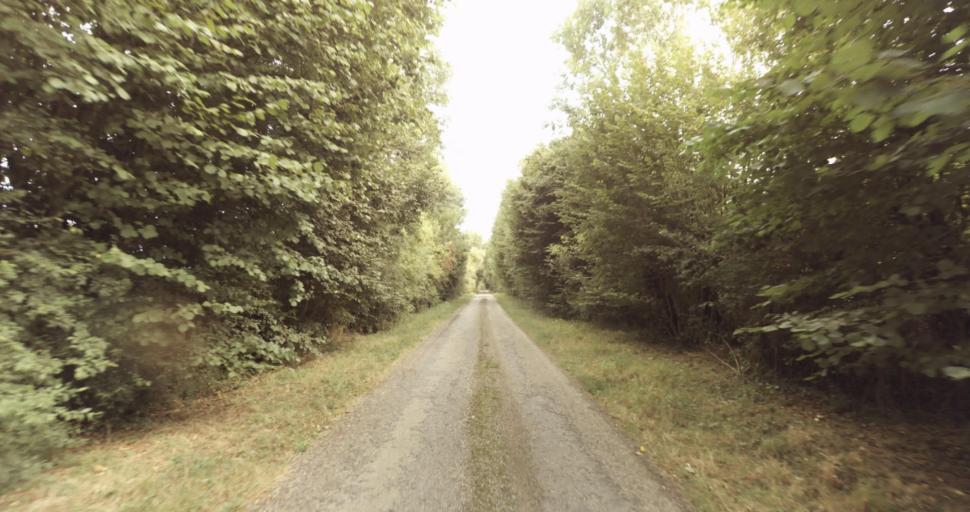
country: FR
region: Lower Normandy
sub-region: Departement de l'Orne
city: Vimoutiers
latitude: 48.9361
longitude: 0.2749
